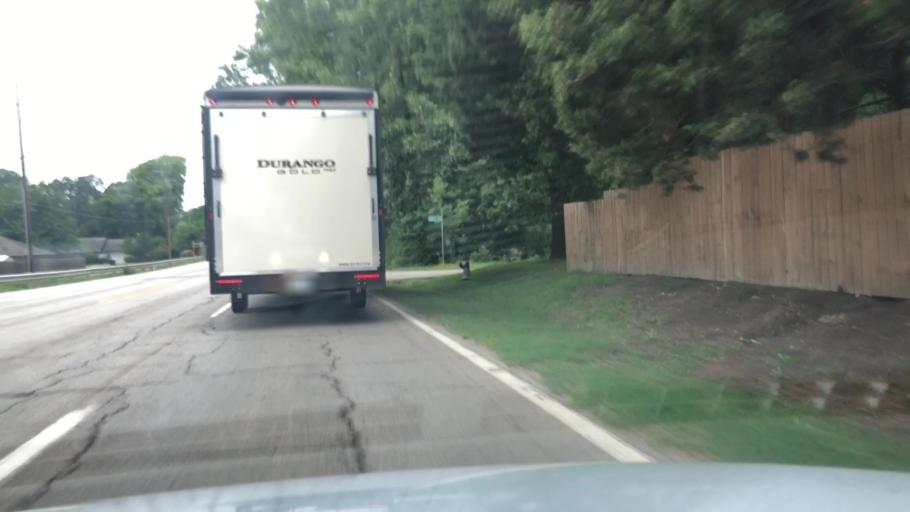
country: US
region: Oklahoma
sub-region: Washington County
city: Bartlesville
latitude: 36.7281
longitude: -95.9134
